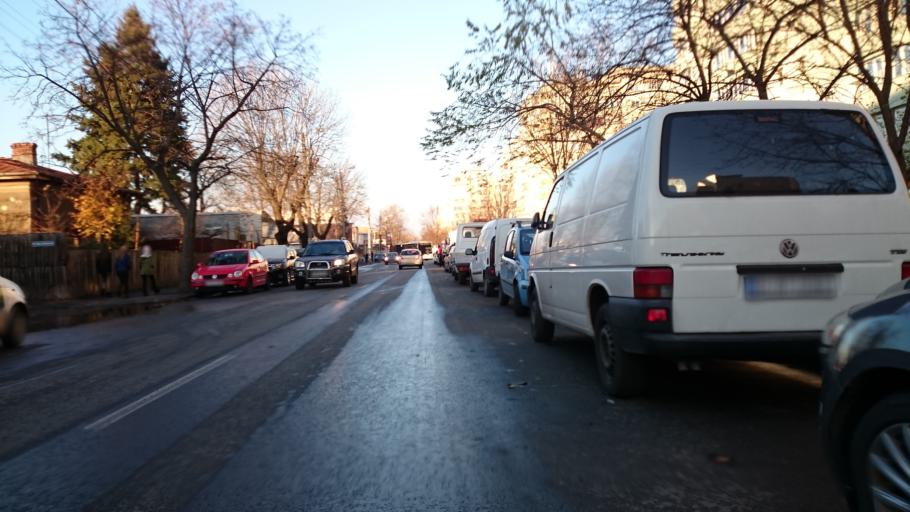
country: RO
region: Bucuresti
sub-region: Municipiul Bucuresti
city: Bucuresti
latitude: 44.4068
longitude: 26.0585
